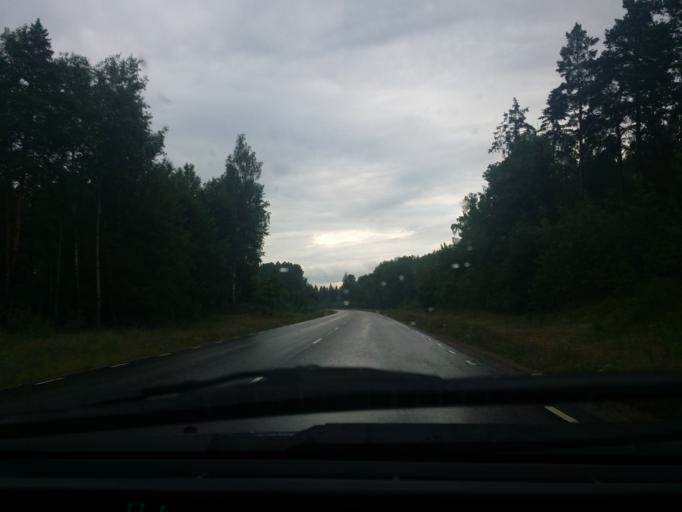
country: SE
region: Vaestmanland
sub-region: Arboga Kommun
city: Arboga
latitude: 59.4145
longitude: 15.8338
